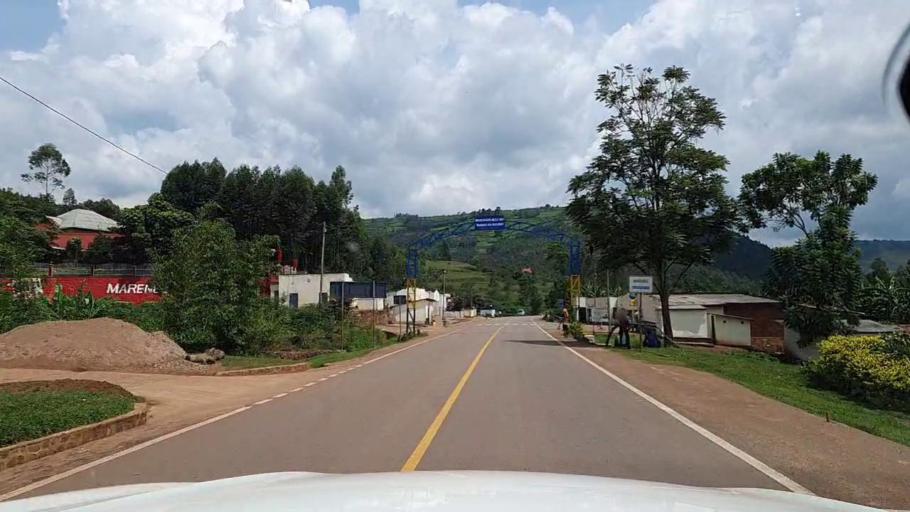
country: RW
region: Kigali
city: Kigali
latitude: -1.8264
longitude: 30.0794
